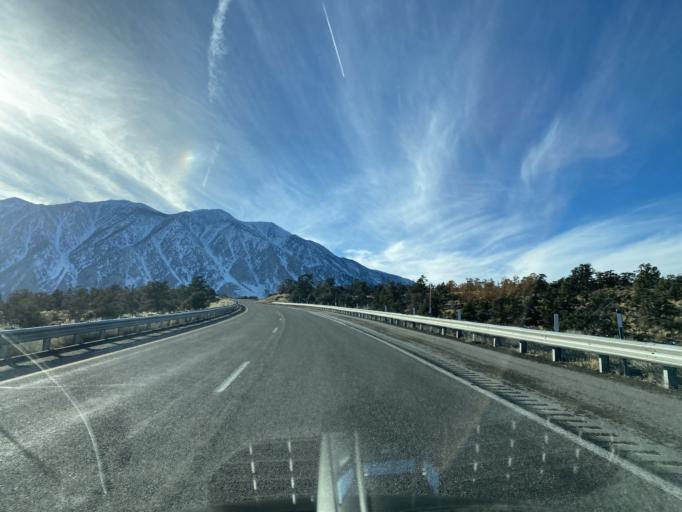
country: US
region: California
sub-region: Inyo County
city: West Bishop
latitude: 37.5208
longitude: -118.6044
